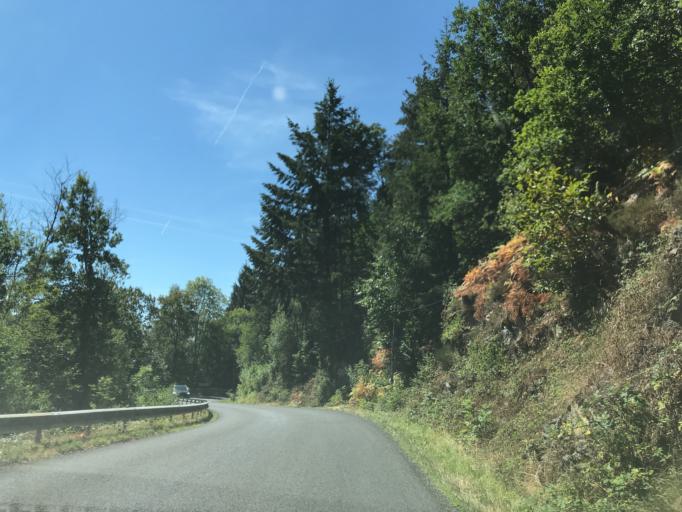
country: FR
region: Auvergne
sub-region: Departement du Puy-de-Dome
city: Courpiere
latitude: 45.7362
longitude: 3.6460
